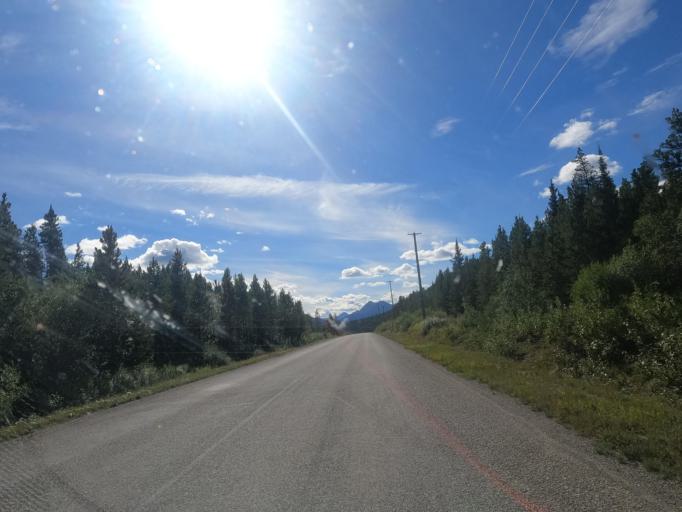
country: CA
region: Yukon
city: Watson Lake
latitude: 59.2741
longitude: -129.5606
